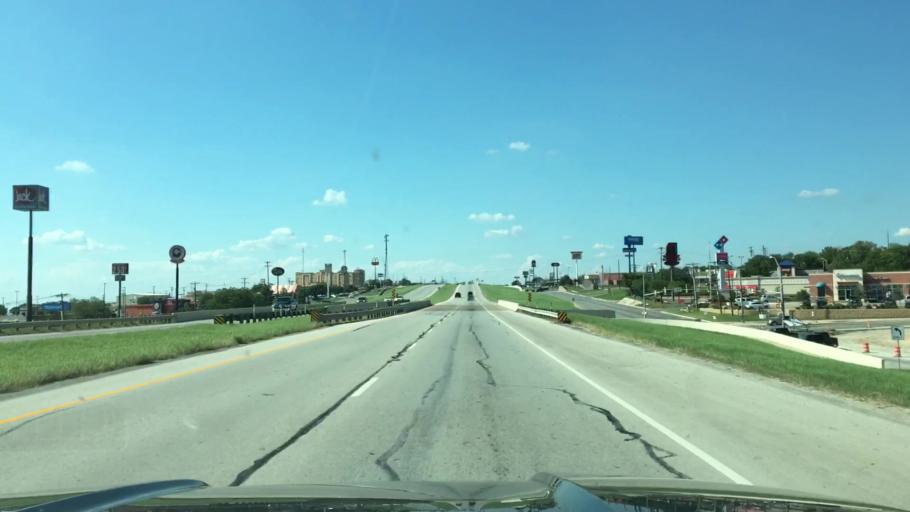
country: US
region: Texas
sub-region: Wise County
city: Decatur
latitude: 33.2270
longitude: -97.5927
